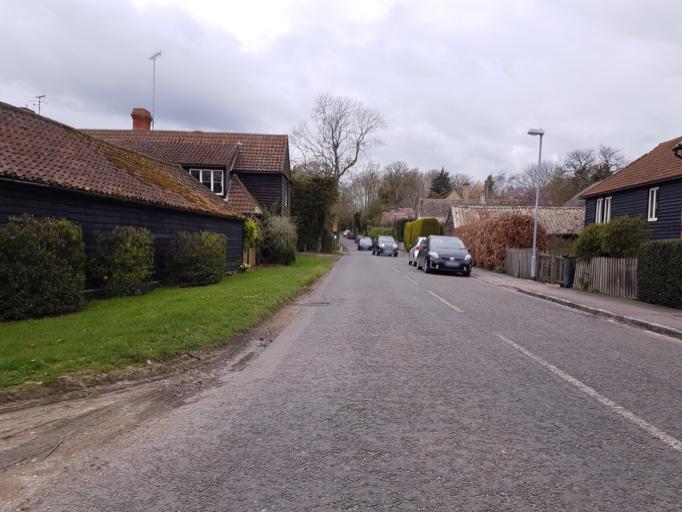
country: GB
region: England
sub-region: Cambridgeshire
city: Girton
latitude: 52.2224
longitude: 0.0463
